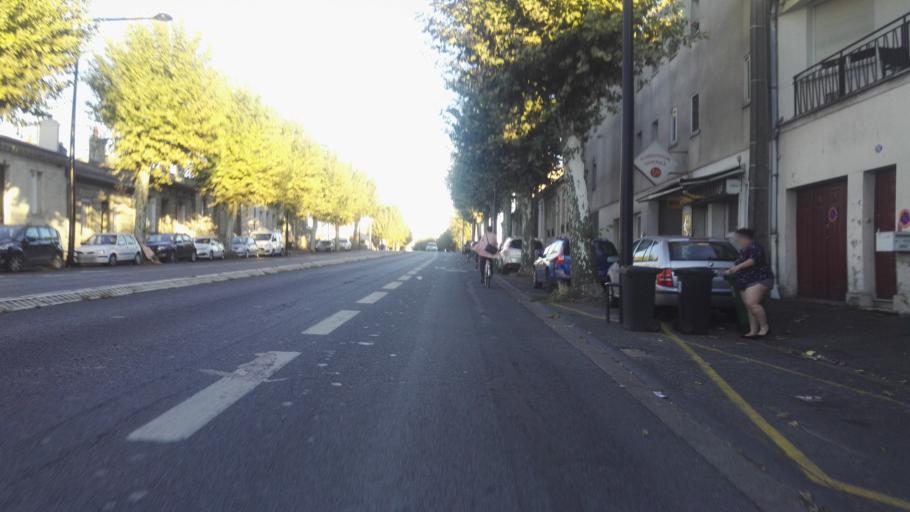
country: FR
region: Aquitaine
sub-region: Departement de la Gironde
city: Begles
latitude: 44.8128
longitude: -0.5609
